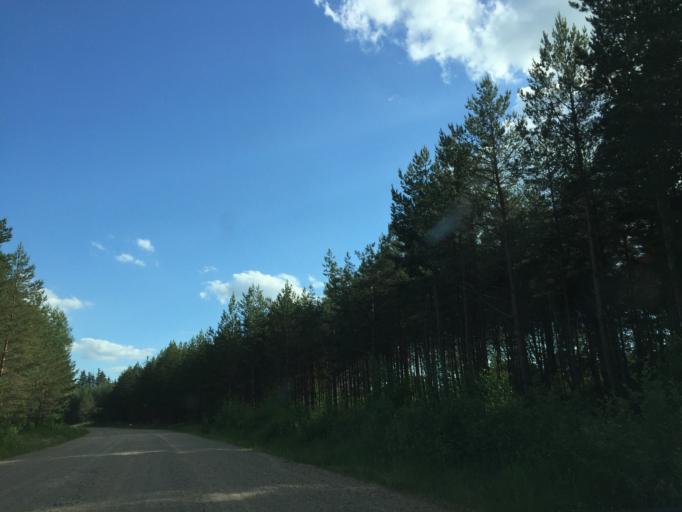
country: LV
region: Kandava
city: Kandava
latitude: 56.8540
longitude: 22.7498
